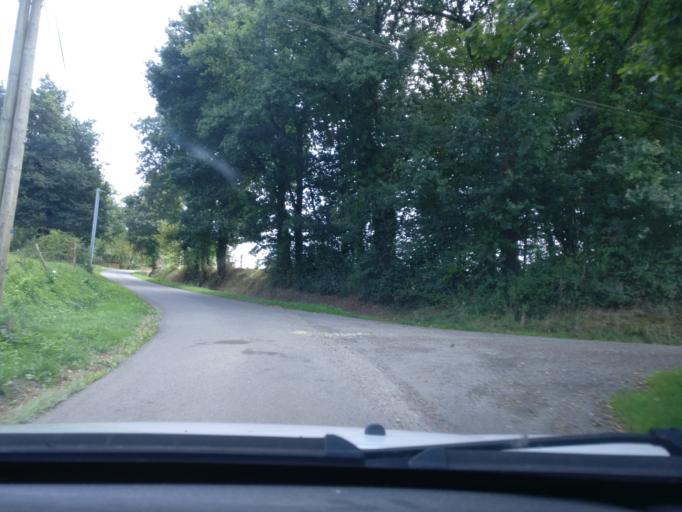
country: FR
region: Brittany
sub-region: Departement d'Ille-et-Vilaine
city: Erce-pres-Liffre
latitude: 48.2685
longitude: -1.5313
